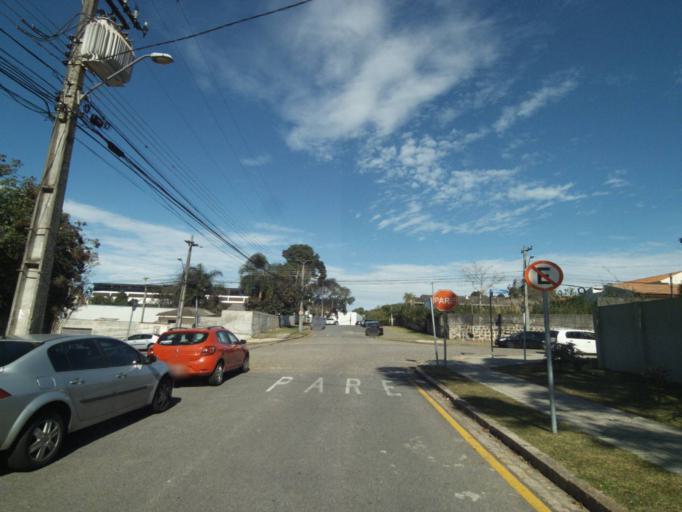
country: BR
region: Parana
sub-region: Curitiba
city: Curitiba
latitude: -25.4137
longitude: -49.2750
